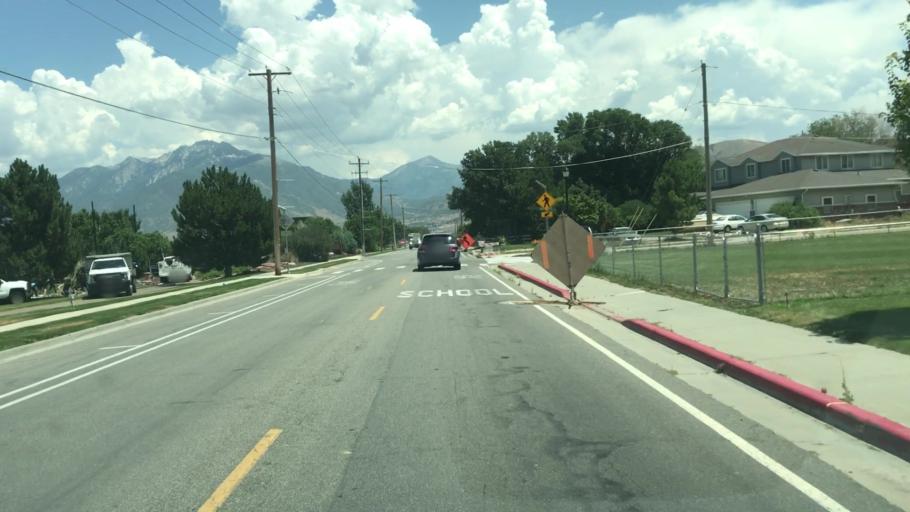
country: US
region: Utah
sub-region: Salt Lake County
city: Bluffdale
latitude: 40.4896
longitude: -111.9527
